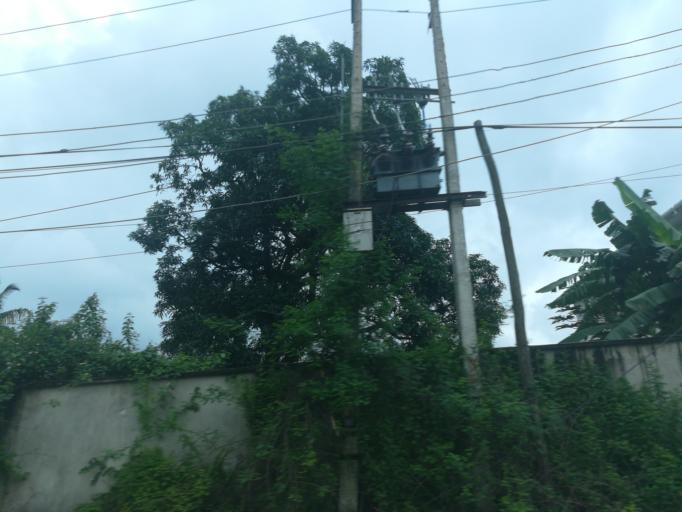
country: NG
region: Lagos
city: Ikeja
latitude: 6.6079
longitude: 3.3418
